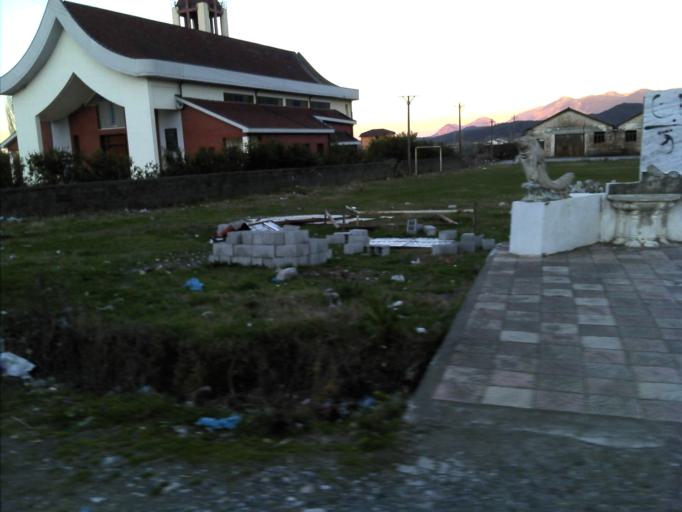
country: AL
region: Shkoder
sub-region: Rrethi i Shkodres
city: Berdica e Madhe
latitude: 42.0165
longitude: 19.4846
